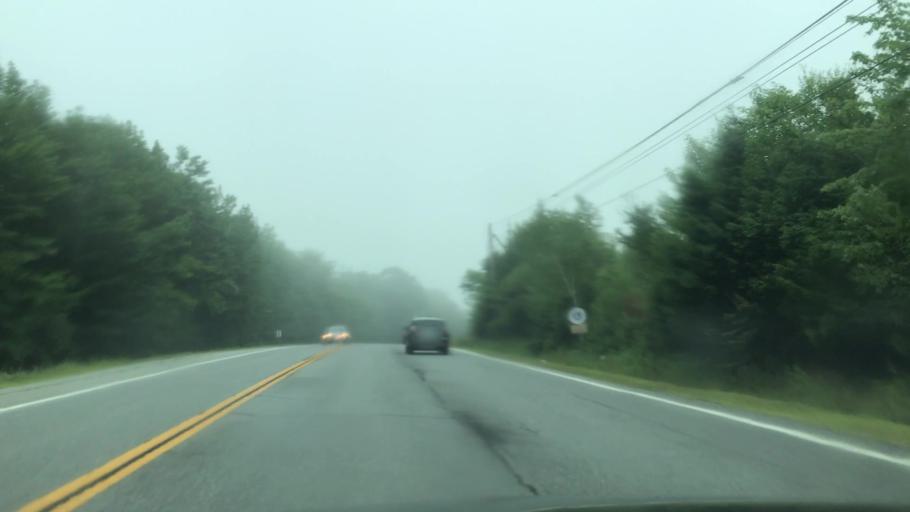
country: US
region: Maine
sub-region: Lincoln County
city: Waldoboro
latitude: 44.0998
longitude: -69.4174
